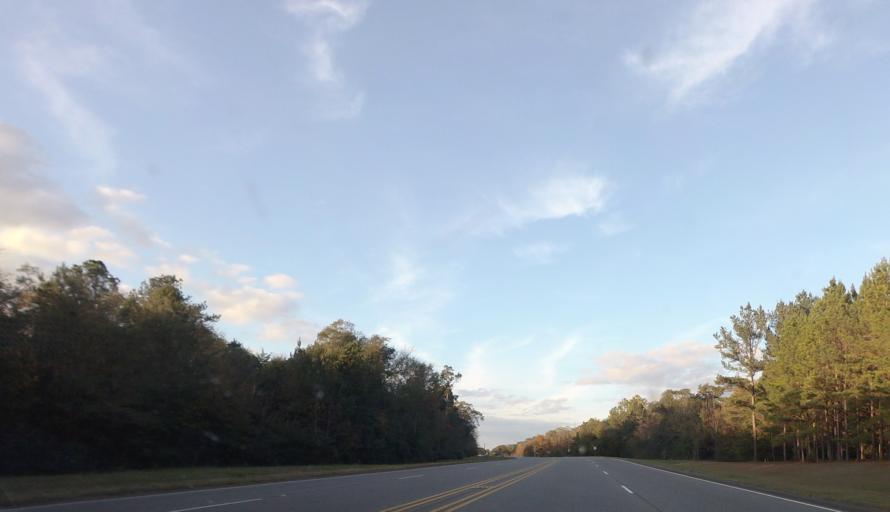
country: US
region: Georgia
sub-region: Houston County
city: Robins Air Force Base
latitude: 32.5394
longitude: -83.4405
